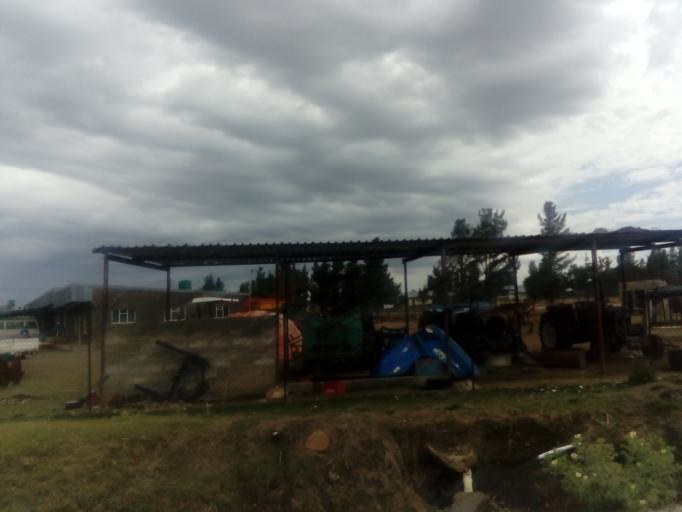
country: LS
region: Leribe
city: Maputsoe
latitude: -28.9365
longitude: 27.9417
